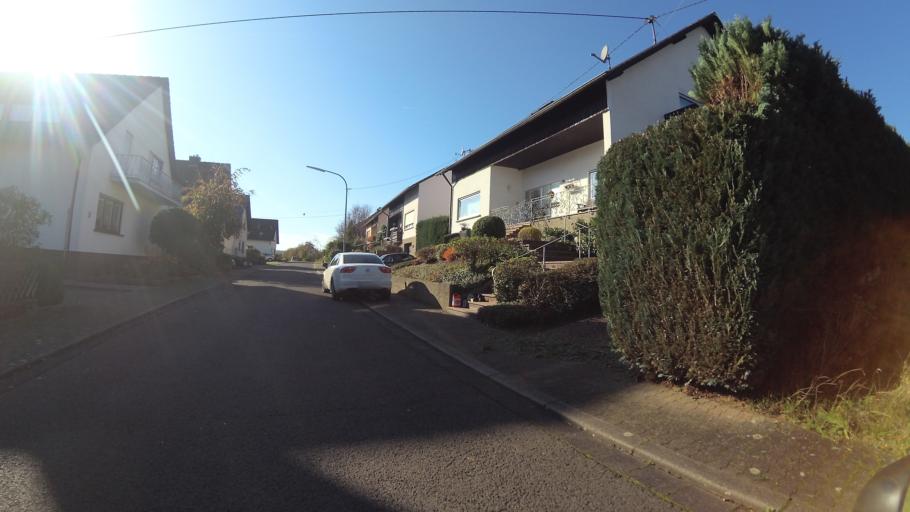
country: DE
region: Saarland
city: Britten
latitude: 49.4801
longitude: 6.7007
